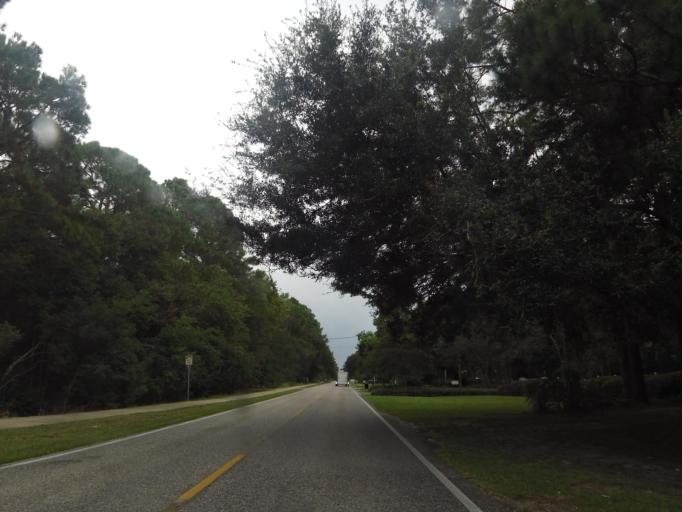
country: US
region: Alabama
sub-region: Baldwin County
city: Point Clear
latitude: 30.4337
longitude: -87.9110
